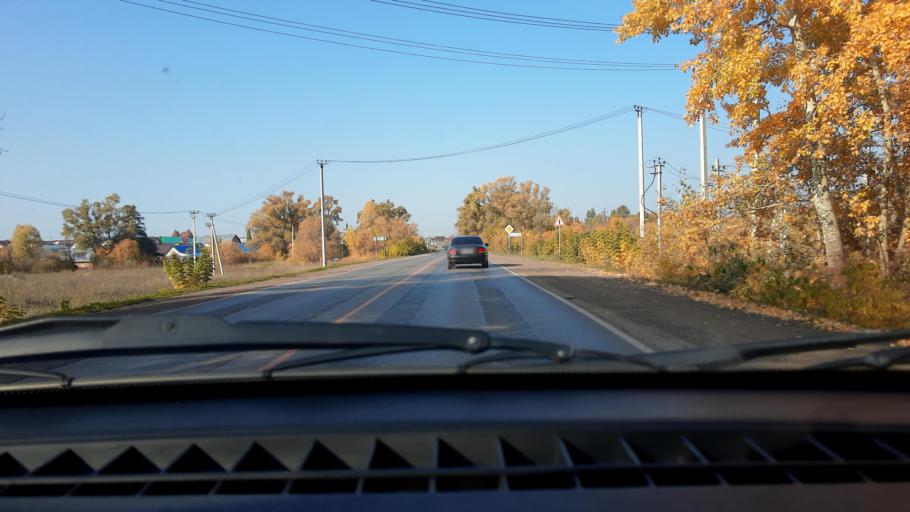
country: RU
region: Bashkortostan
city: Avdon
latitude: 54.7327
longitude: 55.8041
